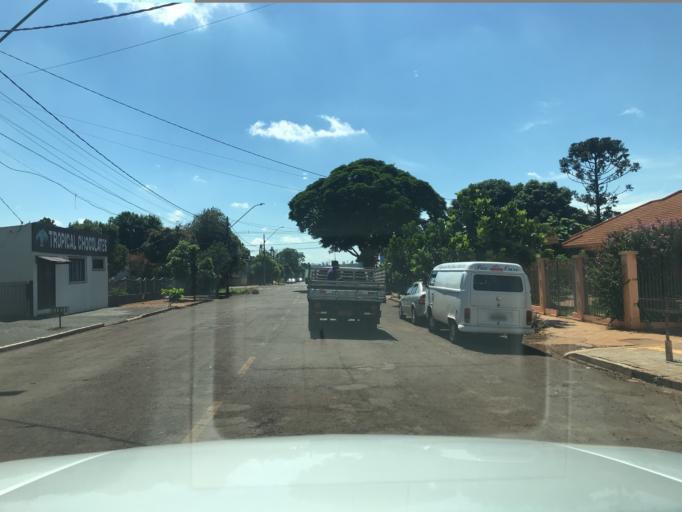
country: BR
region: Parana
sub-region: Palotina
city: Palotina
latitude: -24.2841
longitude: -53.8345
